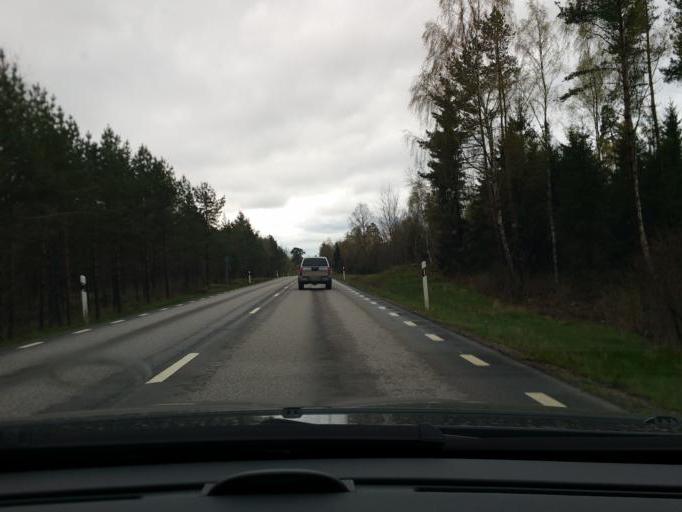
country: SE
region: Kronoberg
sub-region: Vaxjo Kommun
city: Vaexjoe
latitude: 56.8414
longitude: 14.8604
